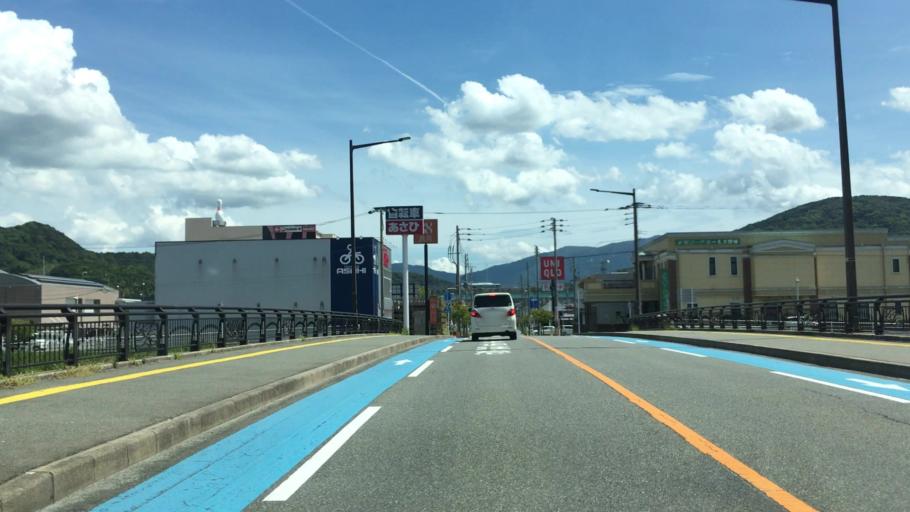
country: JP
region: Fukuoka
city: Onojo
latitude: 33.5445
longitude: 130.4802
